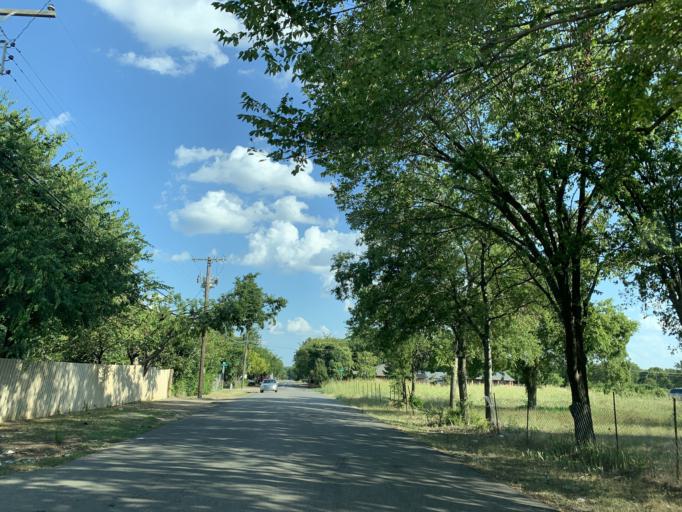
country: US
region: Texas
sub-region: Dallas County
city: Hutchins
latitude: 32.6989
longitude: -96.7815
